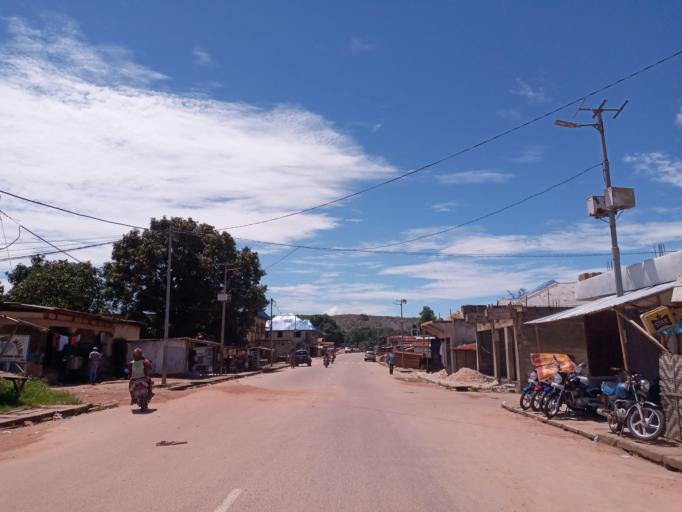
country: SL
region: Eastern Province
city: Koidu
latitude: 8.6418
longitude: -10.9703
